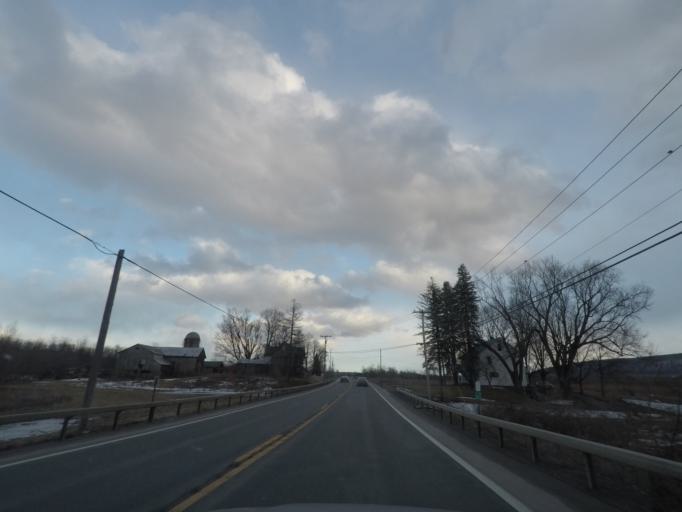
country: US
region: New York
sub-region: Herkimer County
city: Frankfort
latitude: 43.0897
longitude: -75.1301
